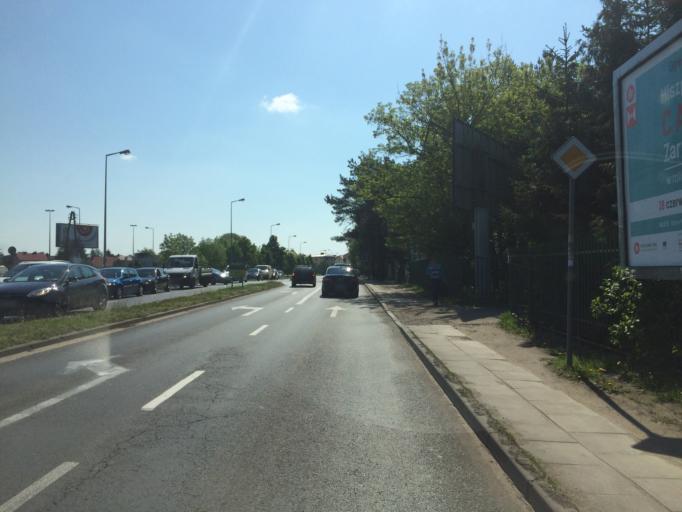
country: PL
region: Masovian Voivodeship
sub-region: Powiat wolominski
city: Zabki
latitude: 52.3027
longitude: 21.0905
